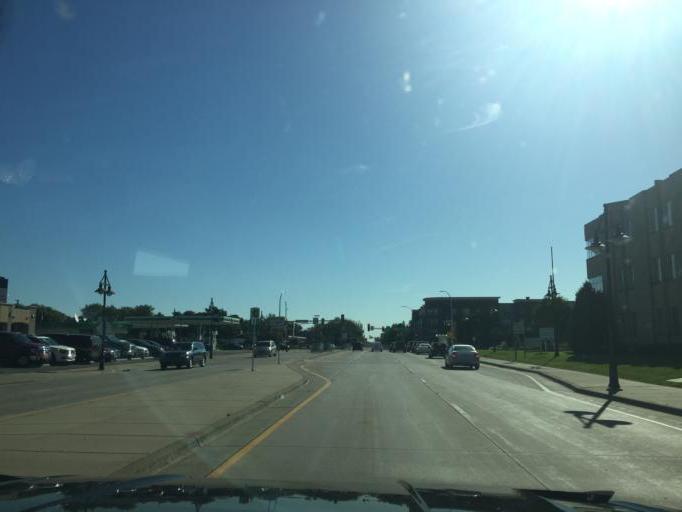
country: US
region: Minnesota
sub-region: Ramsey County
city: Falcon Heights
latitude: 44.9917
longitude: -93.1684
